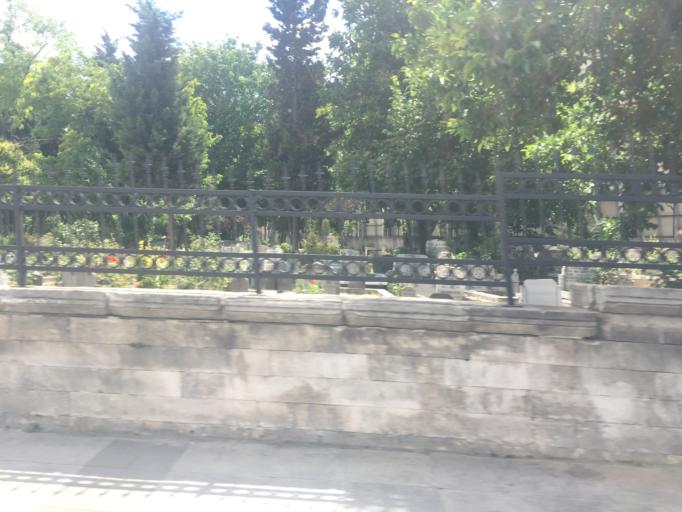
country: TR
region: Istanbul
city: merter keresteciler
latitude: 41.0279
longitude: 28.9175
